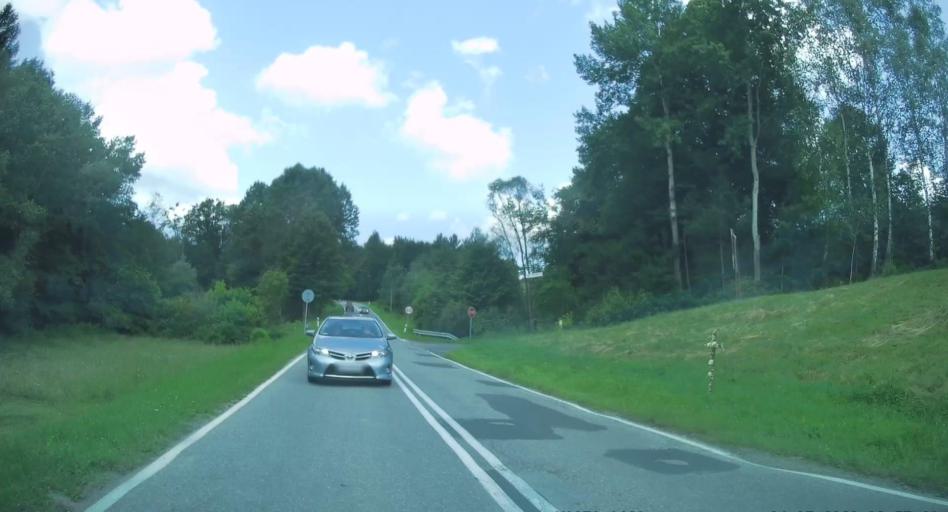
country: PL
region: Lesser Poland Voivodeship
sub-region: Powiat nowosadecki
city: Korzenna
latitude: 49.7618
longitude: 20.7847
